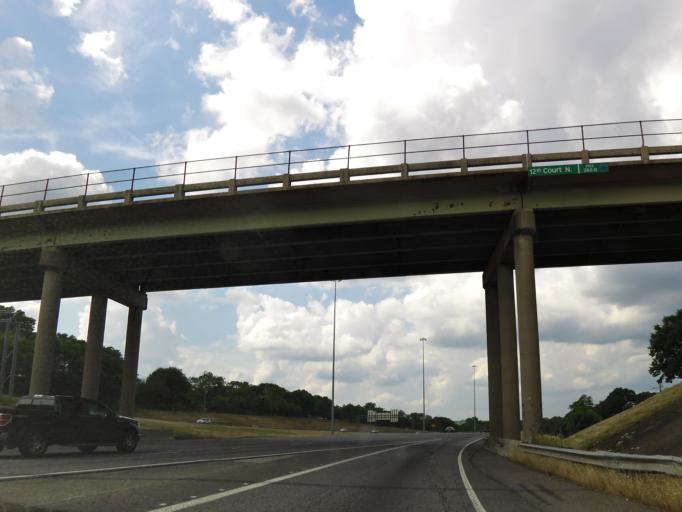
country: US
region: Alabama
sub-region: Jefferson County
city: Birmingham
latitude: 33.5241
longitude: -86.8270
